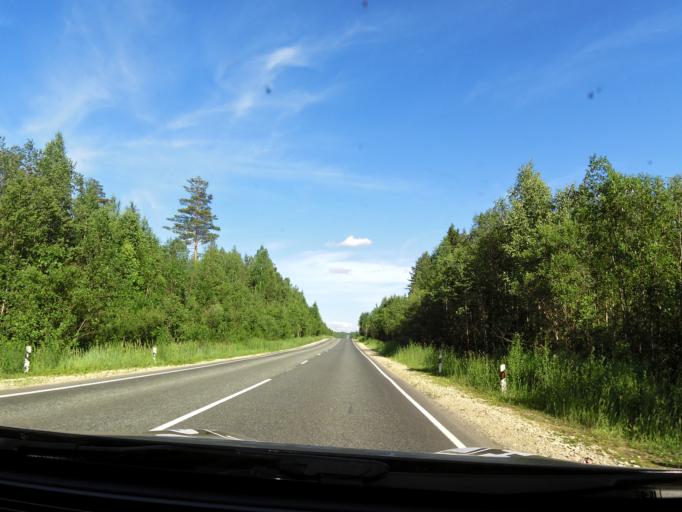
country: RU
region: Kirov
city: Dubrovka
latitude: 58.9077
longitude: 51.2514
